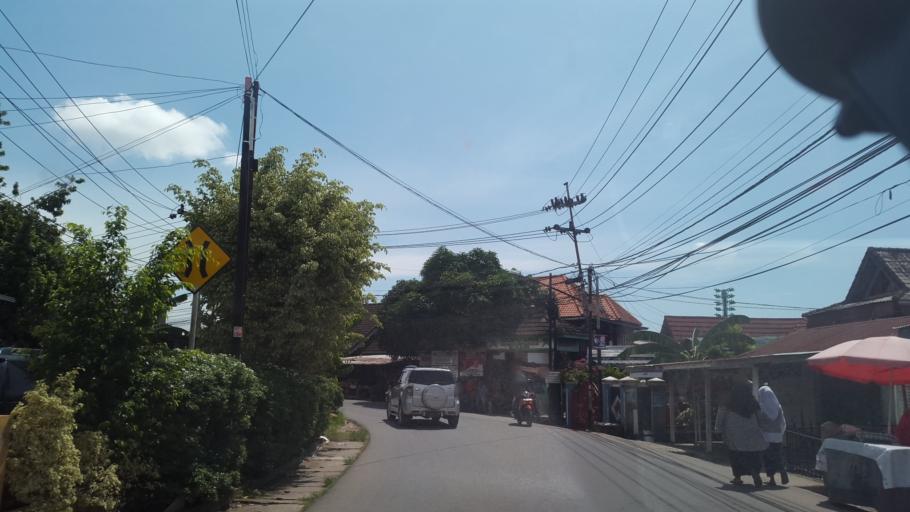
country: ID
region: South Sumatra
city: Plaju
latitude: -3.0028
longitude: 104.7304
